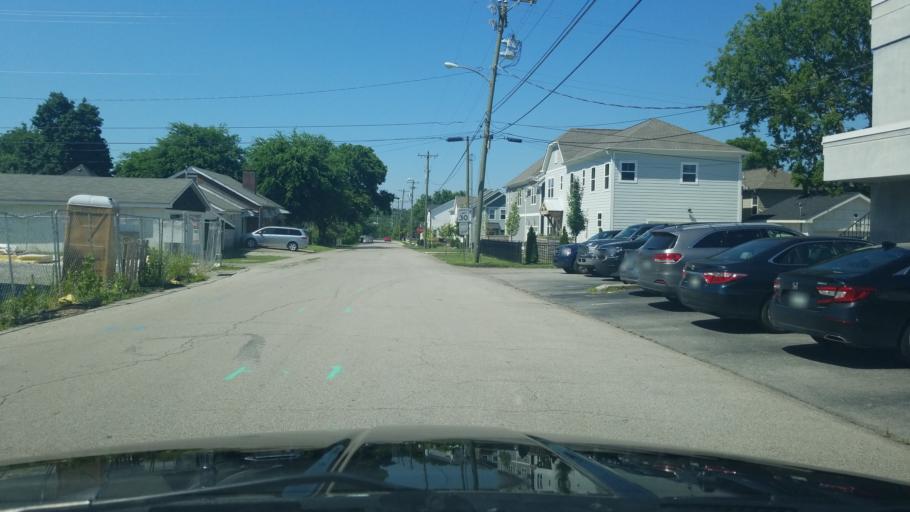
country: US
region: Tennessee
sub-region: Davidson County
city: Belle Meade
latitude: 36.1682
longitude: -86.8607
